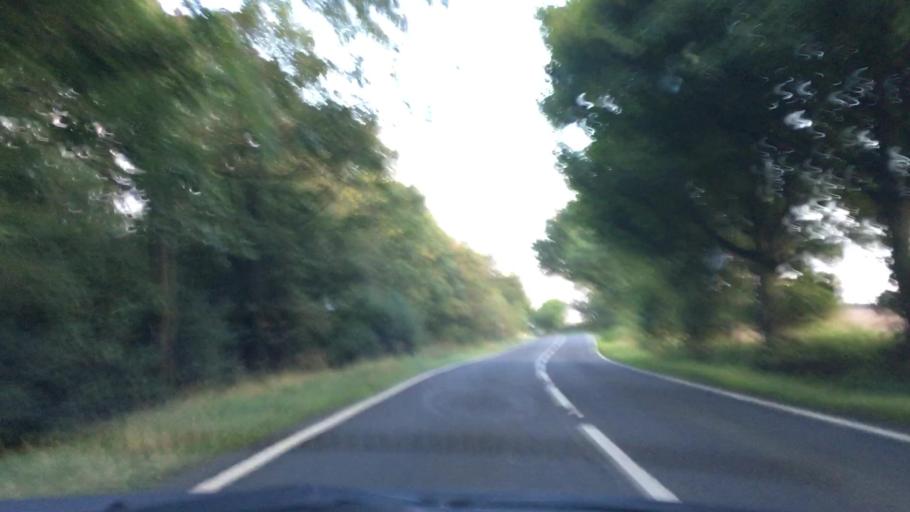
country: GB
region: England
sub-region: North East Lincolnshire
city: Wold Newton
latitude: 53.4781
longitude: -0.1194
